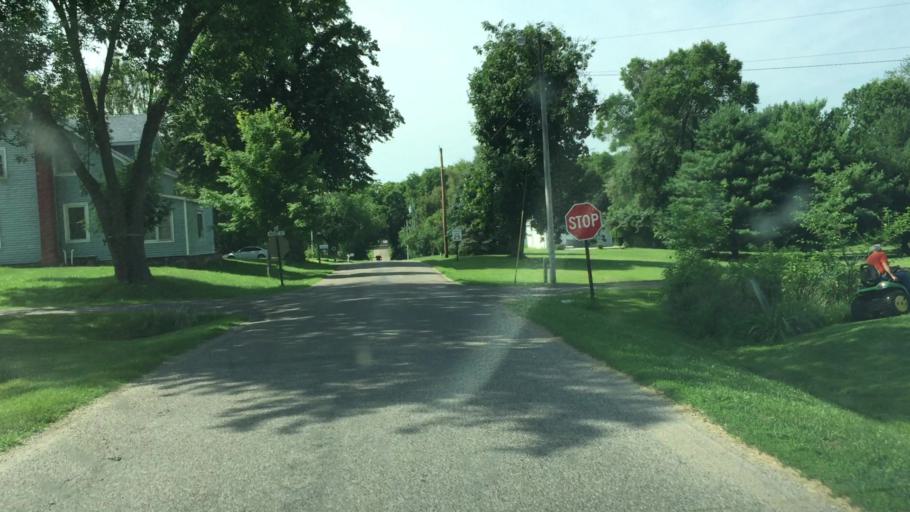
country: US
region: Illinois
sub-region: Hancock County
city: Nauvoo
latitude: 40.5487
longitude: -91.3754
